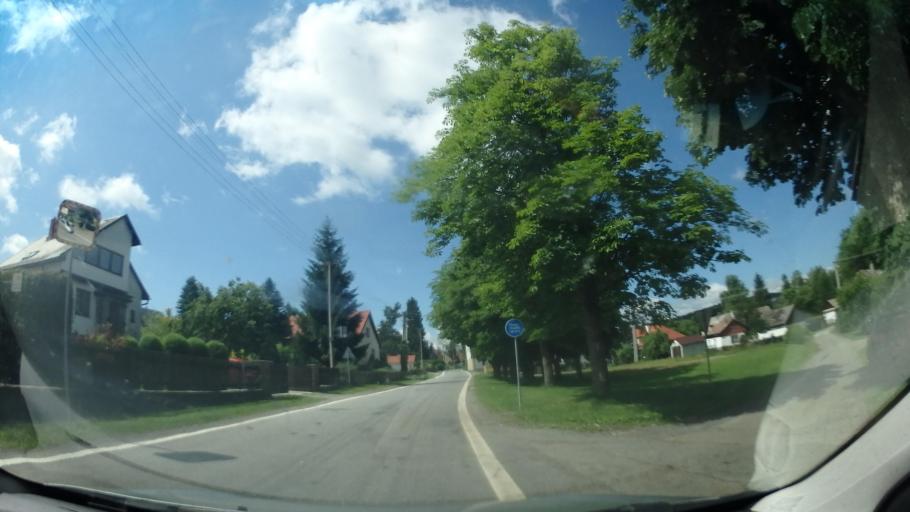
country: CZ
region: Vysocina
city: Heralec
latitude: 49.6280
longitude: 16.0381
